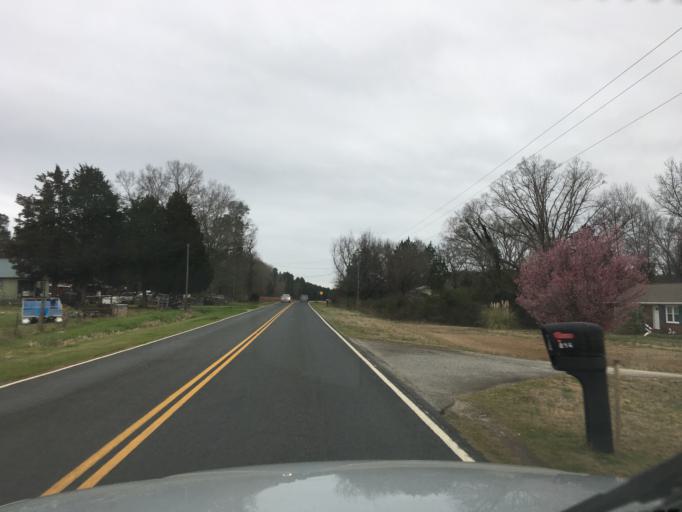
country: US
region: South Carolina
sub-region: Greenwood County
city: Greenwood
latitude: 34.1328
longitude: -82.1552
